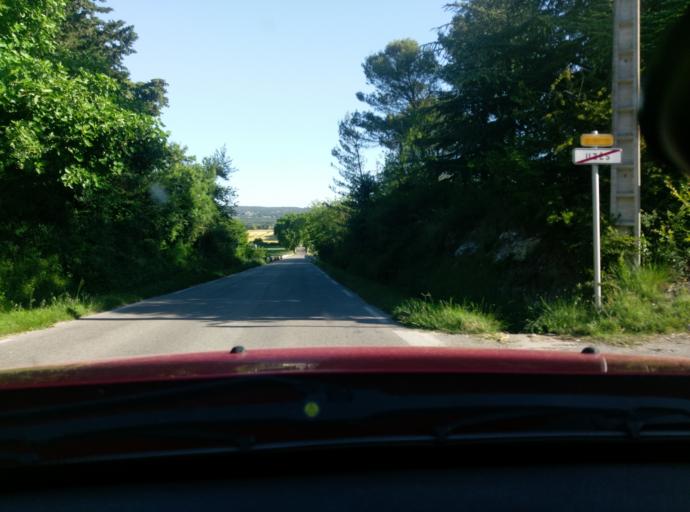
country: FR
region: Languedoc-Roussillon
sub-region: Departement du Gard
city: Uzes
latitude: 44.0287
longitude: 4.4120
